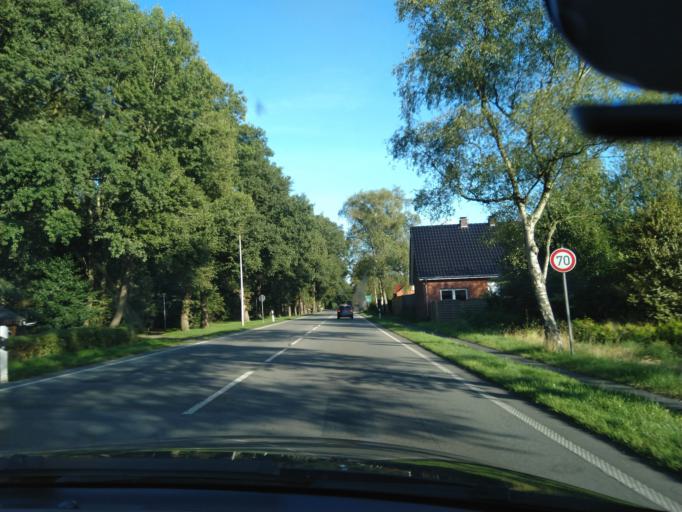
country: DE
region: Lower Saxony
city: Leer
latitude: 53.2376
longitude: 7.4710
